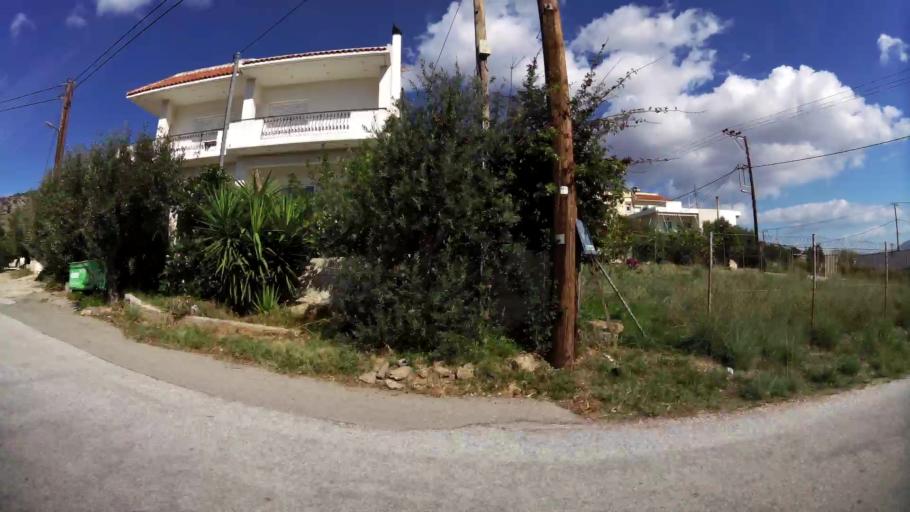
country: GR
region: Attica
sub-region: Nomarchia Anatolikis Attikis
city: Vari
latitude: 37.8421
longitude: 23.7971
